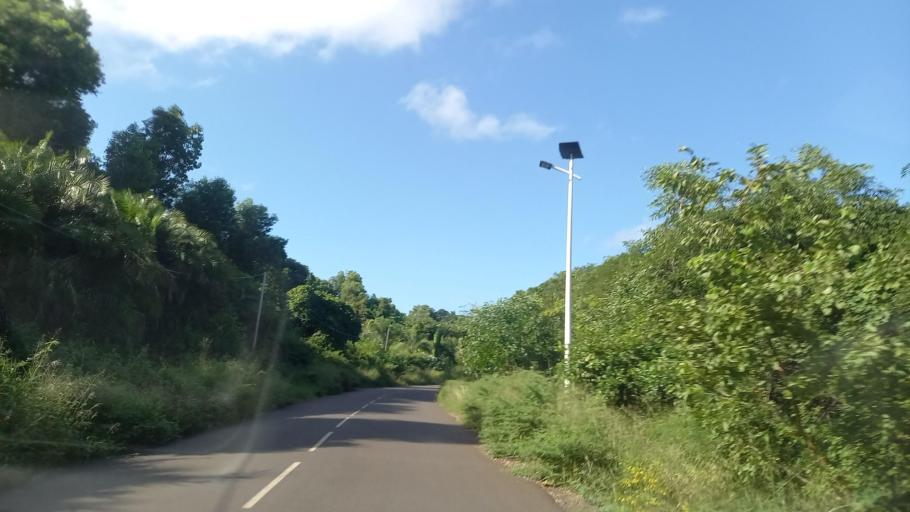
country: YT
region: Kani-Keli
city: Kani Keli
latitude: -12.9828
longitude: 45.1255
